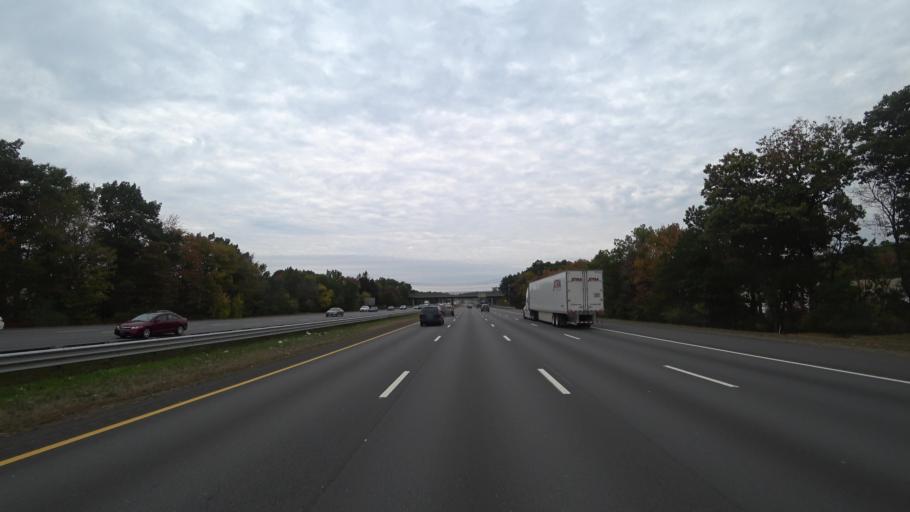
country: US
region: Massachusetts
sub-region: Middlesex County
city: Reading
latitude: 42.5313
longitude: -71.1357
